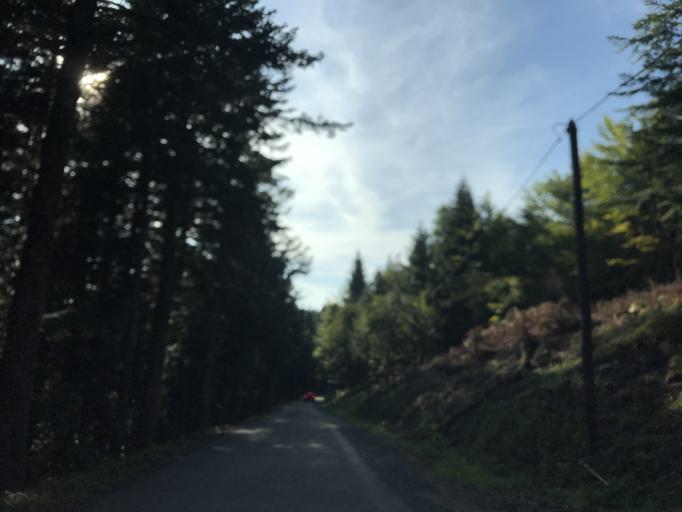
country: FR
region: Auvergne
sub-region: Departement du Puy-de-Dome
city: Job
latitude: 45.6811
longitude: 3.7651
